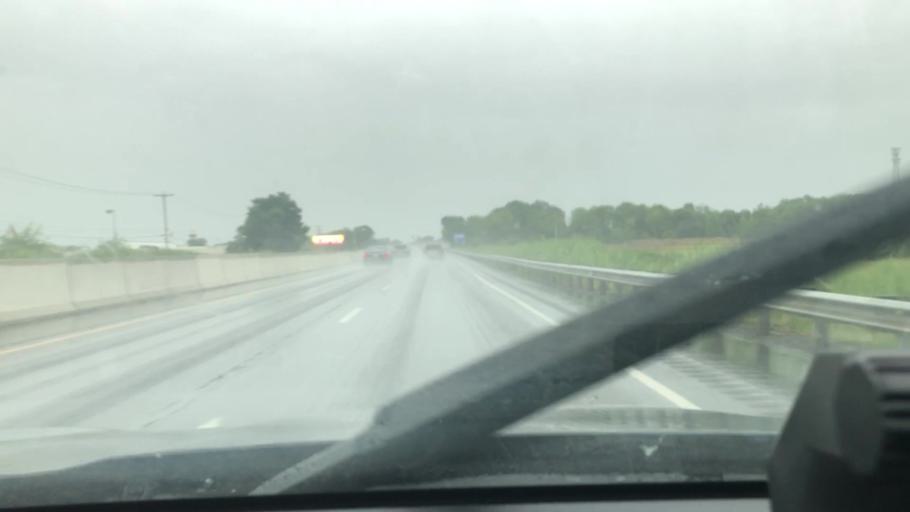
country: US
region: Pennsylvania
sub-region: Northampton County
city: Wind Gap
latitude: 40.8411
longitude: -75.3018
